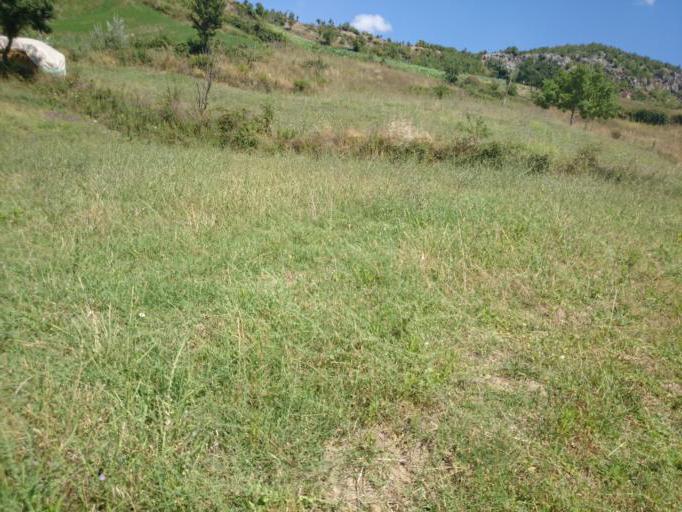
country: AL
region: Elbasan
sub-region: Rrethi i Elbasanit
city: Shushice
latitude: 41.0614
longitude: 20.1462
